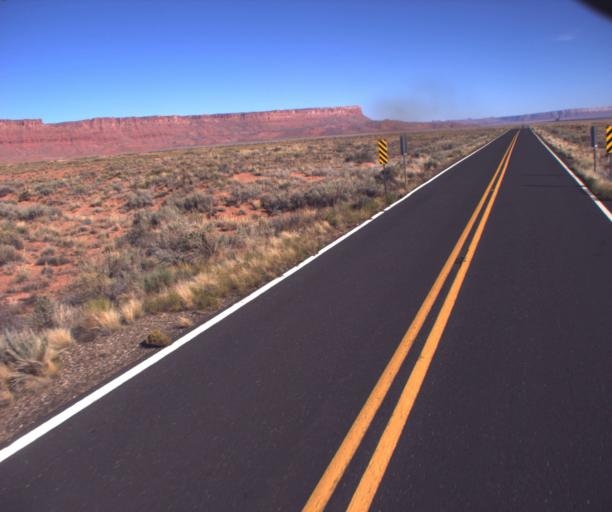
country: US
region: Arizona
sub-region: Coconino County
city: Page
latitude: 36.7136
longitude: -111.9847
